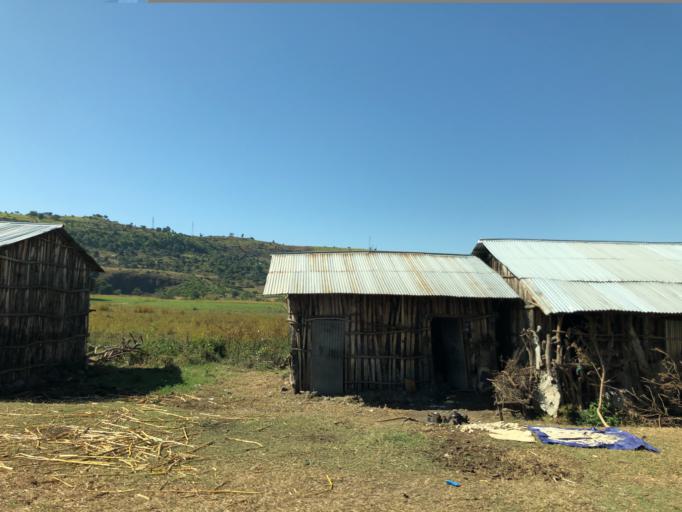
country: ET
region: Amhara
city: Adis Zemen
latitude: 12.1807
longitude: 37.6836
